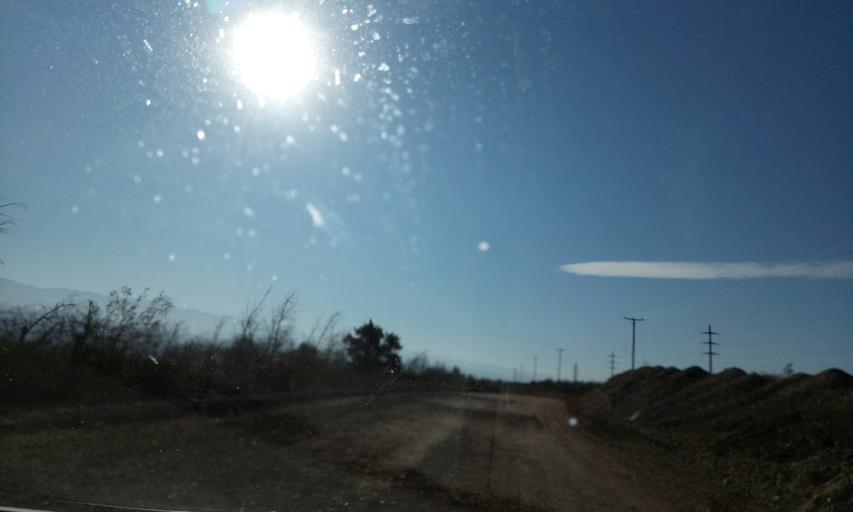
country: AR
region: San Juan
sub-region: Departamento de Rivadavia
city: Rivadavia
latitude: -31.4223
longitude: -68.6684
